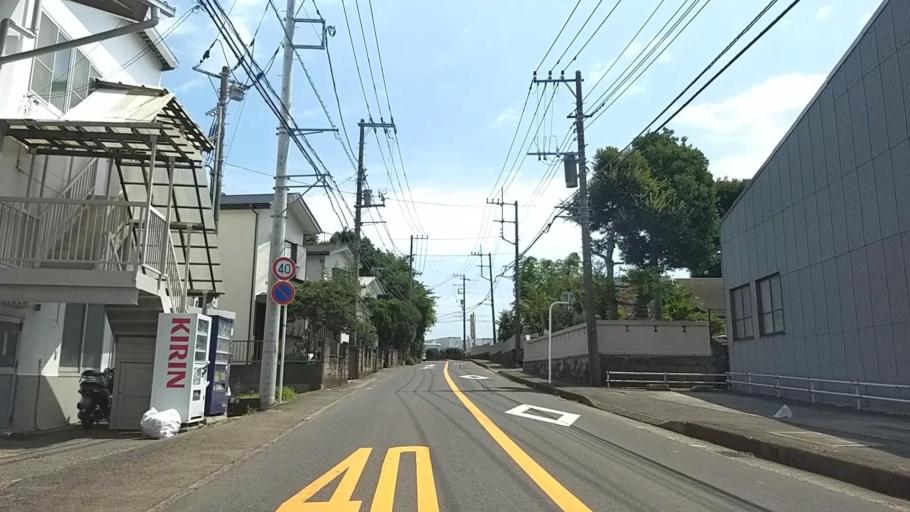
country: JP
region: Kanagawa
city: Fujisawa
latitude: 35.4024
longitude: 139.4375
